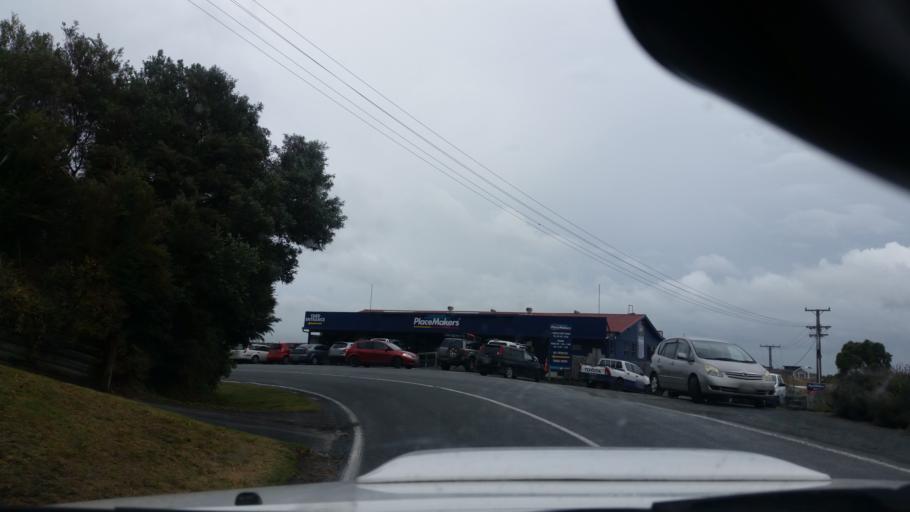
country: NZ
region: Auckland
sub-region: Auckland
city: Wellsford
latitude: -36.1009
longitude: 174.5883
